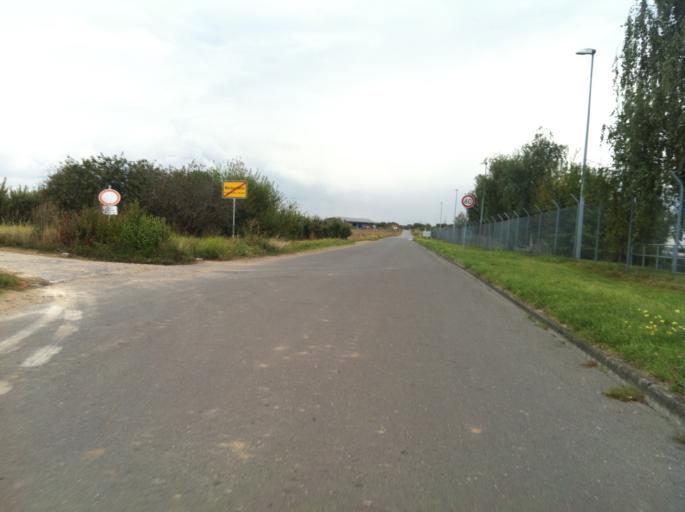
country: DE
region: Rheinland-Pfalz
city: Wackernheim
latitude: 49.9662
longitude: 8.1232
